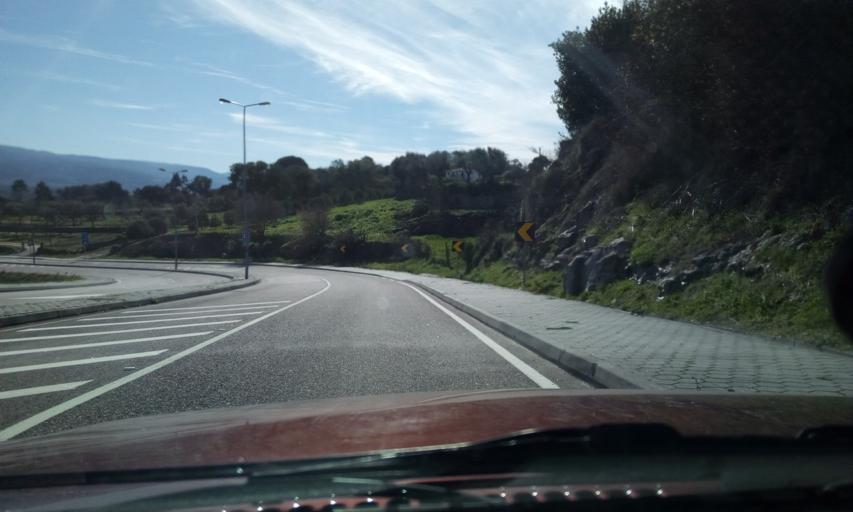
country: PT
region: Guarda
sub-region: Fornos de Algodres
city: Fornos de Algodres
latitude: 40.6165
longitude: -7.5381
